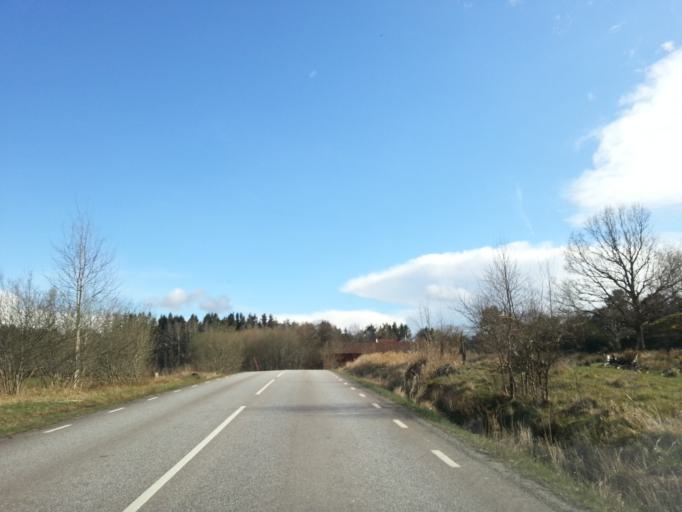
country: SE
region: Vaestra Goetaland
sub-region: Kungalvs Kommun
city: Kode
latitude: 57.9180
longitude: 11.9176
